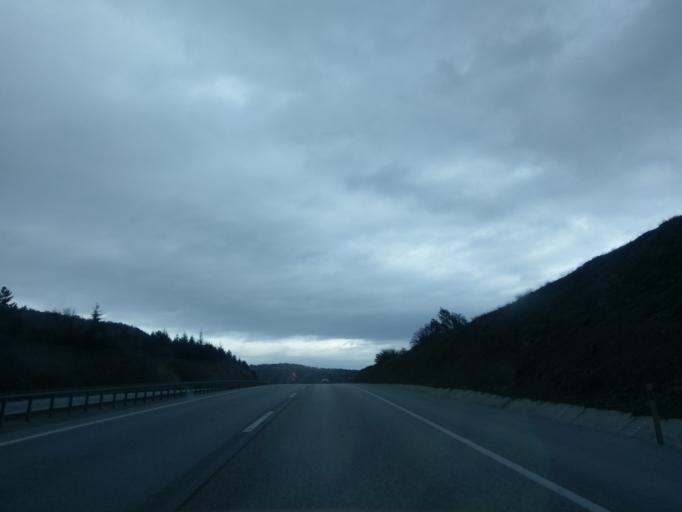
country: TR
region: Kuetahya
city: Sabuncu
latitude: 39.5787
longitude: 30.1207
